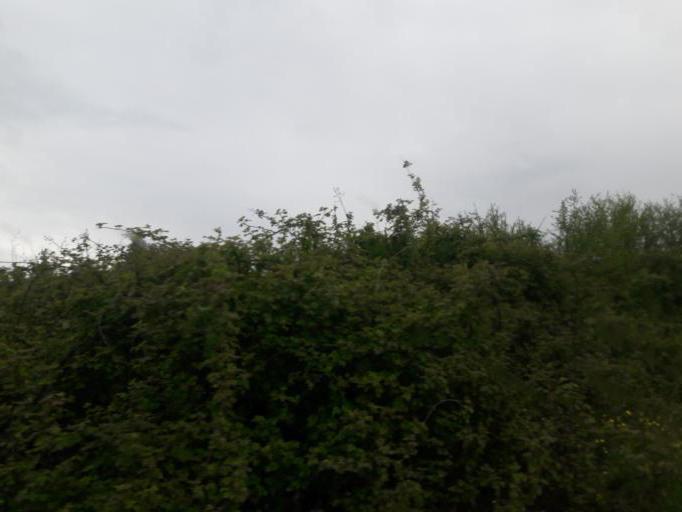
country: AL
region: Shkoder
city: Vukatane
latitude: 42.0122
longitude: 19.5351
